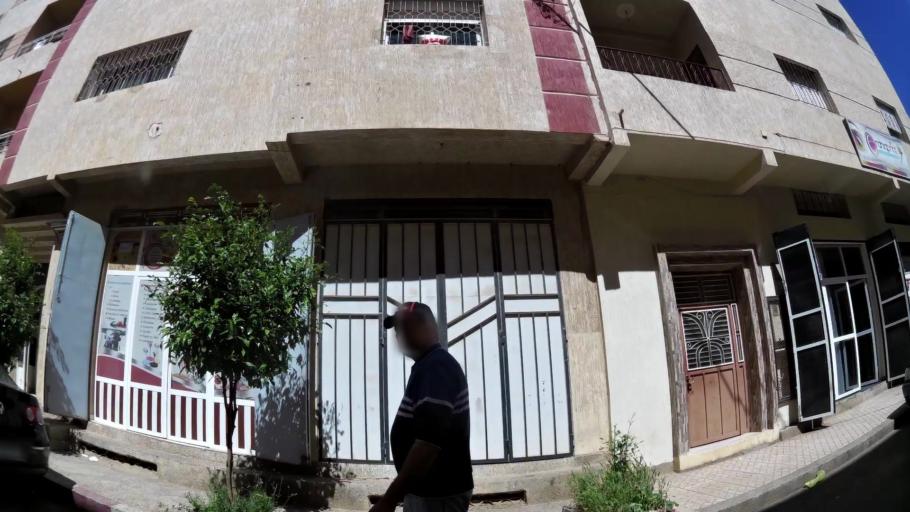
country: MA
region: Meknes-Tafilalet
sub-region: Meknes
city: Meknes
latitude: 33.8684
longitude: -5.5516
